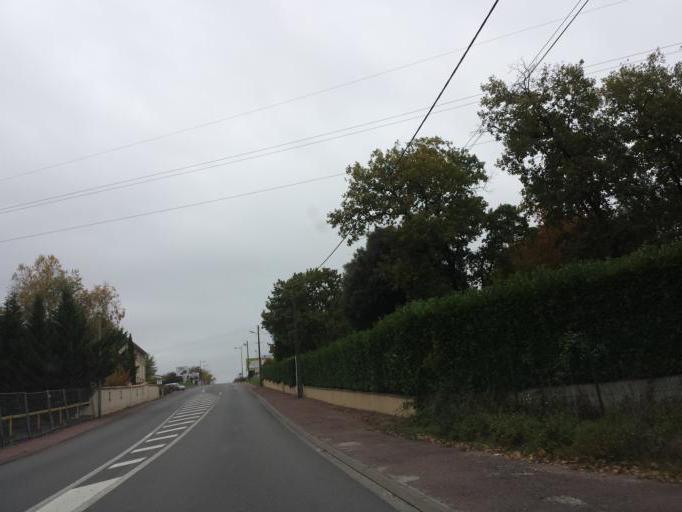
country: FR
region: Poitou-Charentes
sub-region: Departement de la Charente
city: Puymoyen
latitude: 45.6225
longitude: 0.1637
